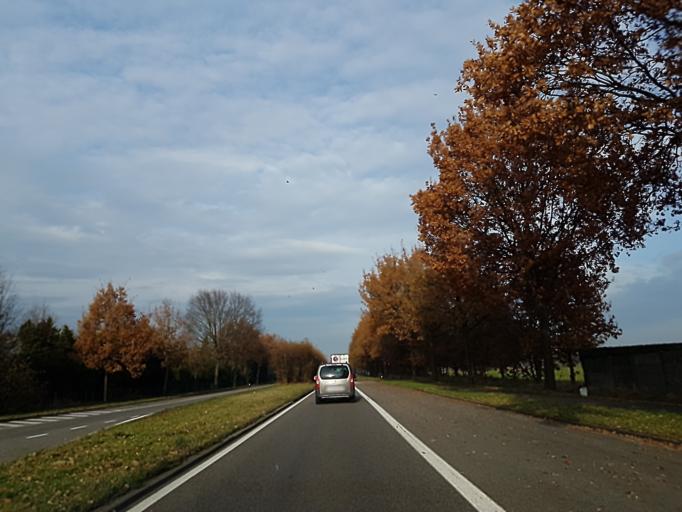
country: BE
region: Flanders
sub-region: Provincie Antwerpen
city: Essen
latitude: 51.4661
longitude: 4.4766
